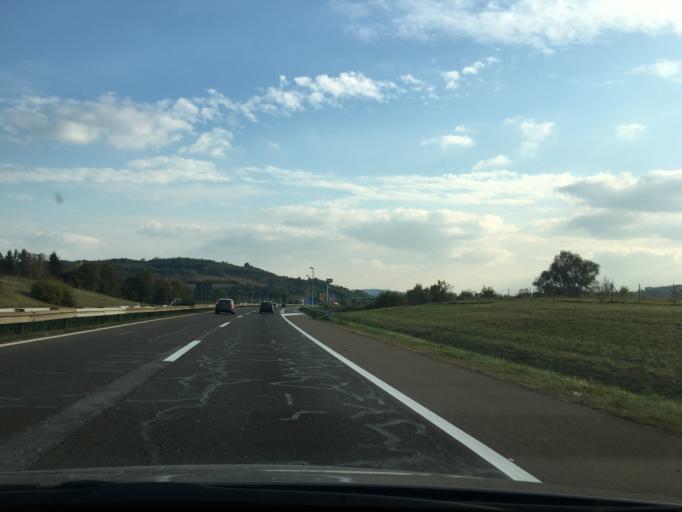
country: RS
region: Central Serbia
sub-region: Belgrade
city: Zvezdara
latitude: 44.6969
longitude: 20.5822
